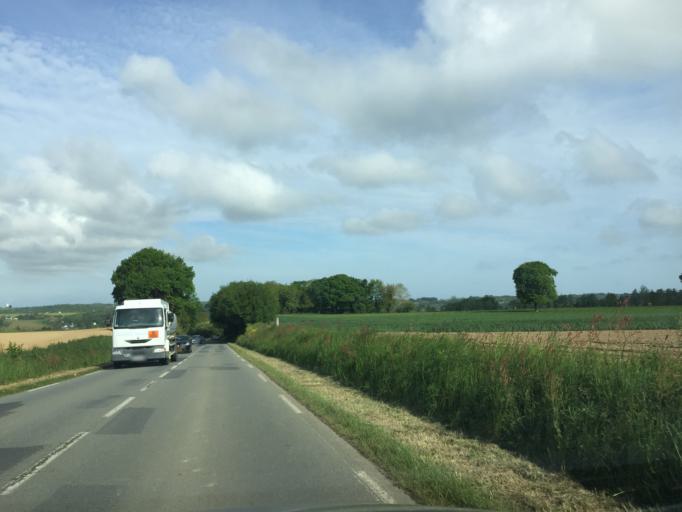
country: FR
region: Brittany
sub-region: Departement des Cotes-d'Armor
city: Matignon
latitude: 48.6075
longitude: -2.3068
